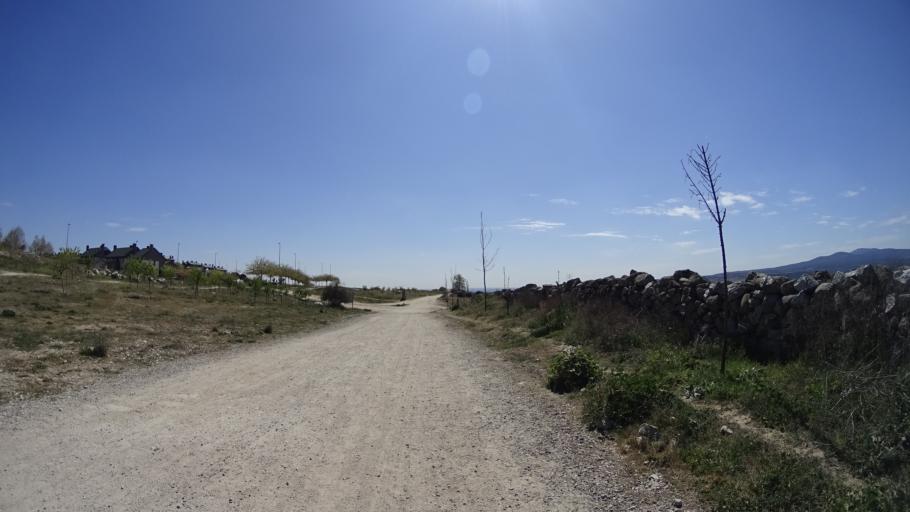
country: ES
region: Madrid
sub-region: Provincia de Madrid
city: Colmenar Viejo
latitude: 40.6665
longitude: -3.7857
